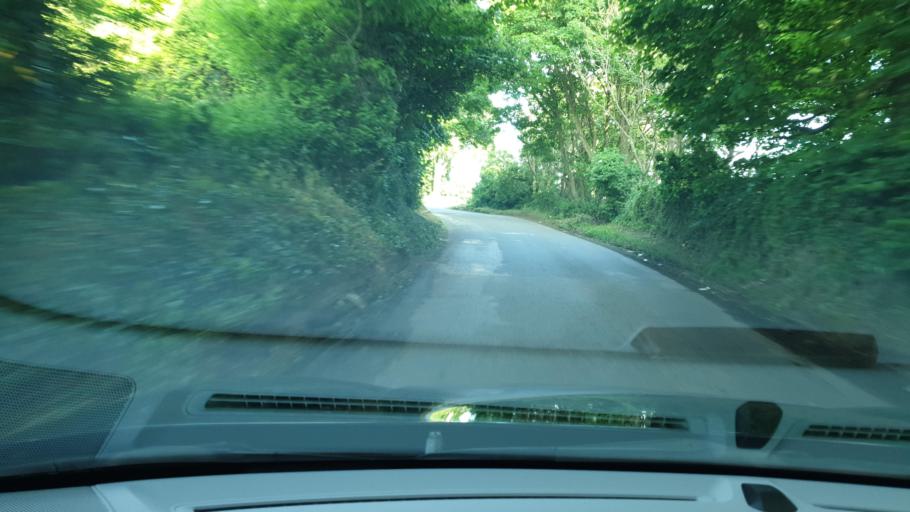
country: IE
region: Leinster
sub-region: An Mhi
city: Ashbourne
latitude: 53.5470
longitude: -6.4069
